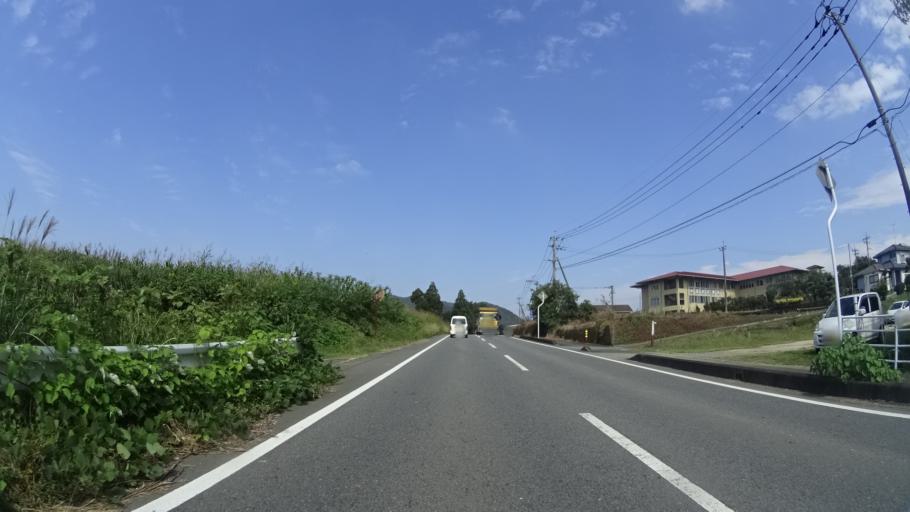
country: JP
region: Kumamoto
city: Matsubase
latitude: 32.6642
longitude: 130.7181
